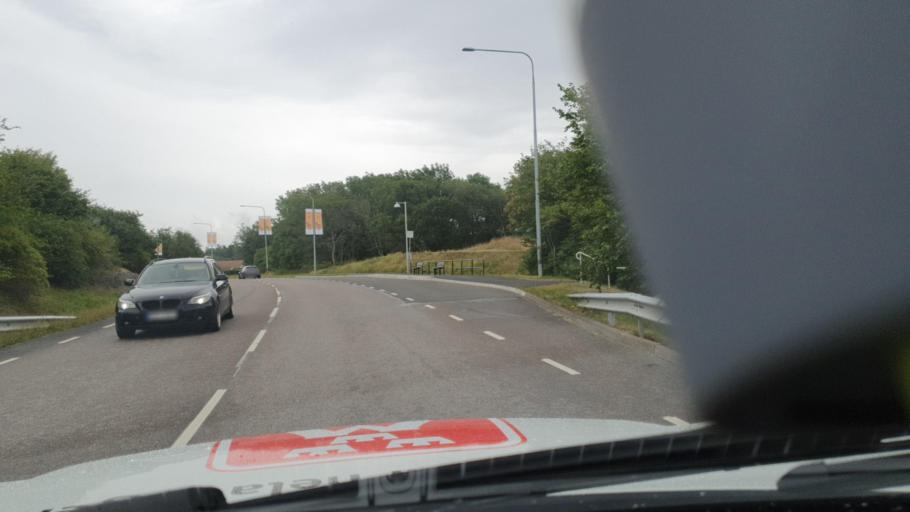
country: SE
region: Vaestra Goetaland
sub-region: Molndal
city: Lindome
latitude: 57.5772
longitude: 12.0954
